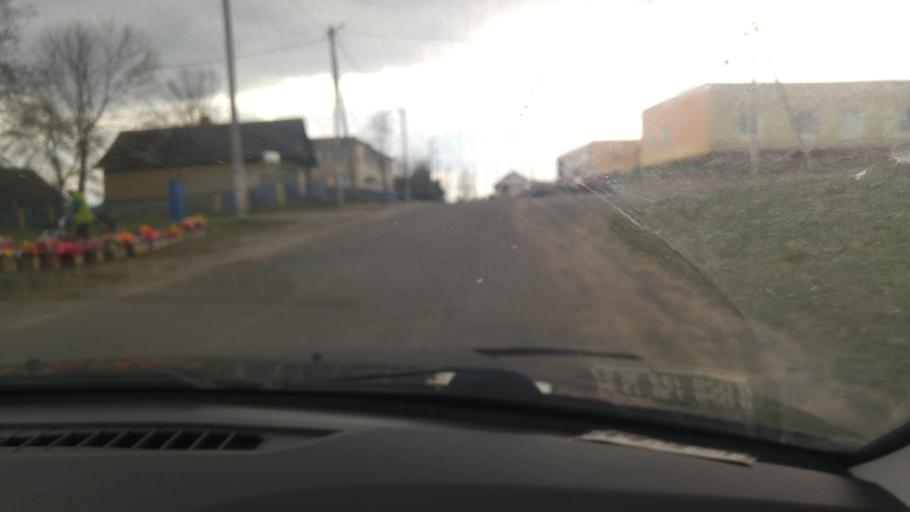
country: BY
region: Minsk
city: Prawdzinski
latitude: 53.4318
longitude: 27.6947
